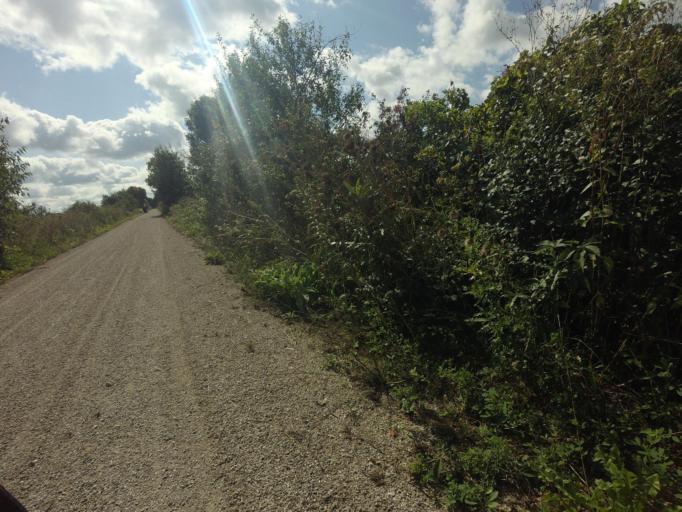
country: CA
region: Ontario
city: Huron East
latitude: 43.7178
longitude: -81.3909
